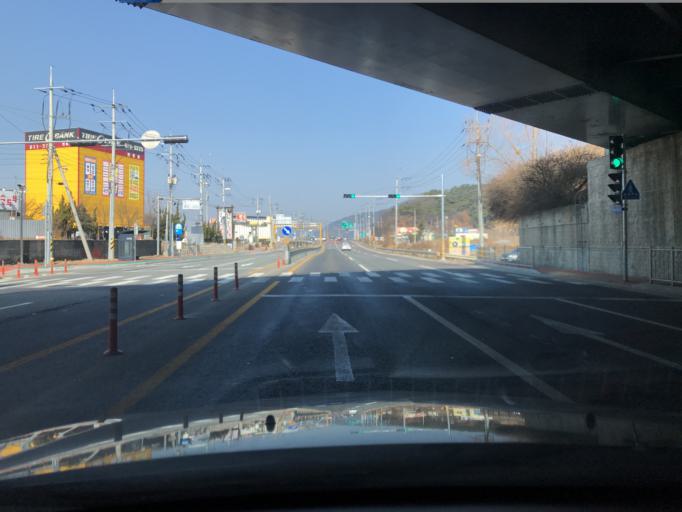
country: KR
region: Daegu
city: Hwawon
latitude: 35.7052
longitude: 128.4380
